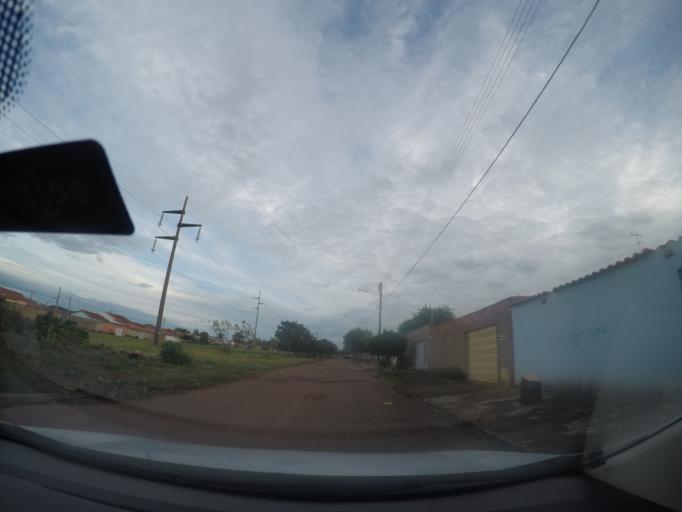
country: BR
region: Goias
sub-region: Goianira
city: Goianira
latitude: -16.5761
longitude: -49.3810
